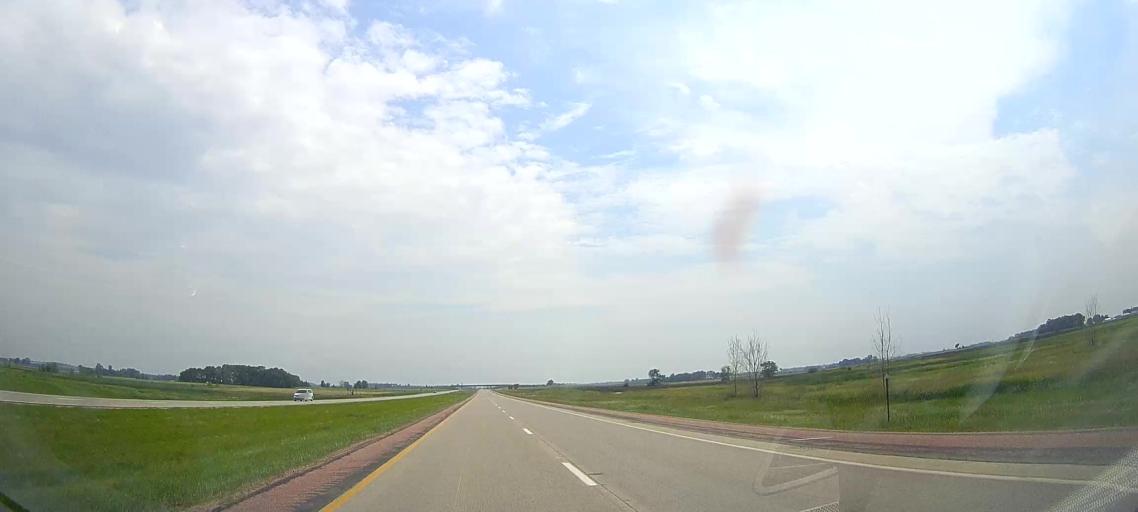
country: US
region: South Dakota
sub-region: Union County
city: Beresford
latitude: 42.9634
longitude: -96.7951
